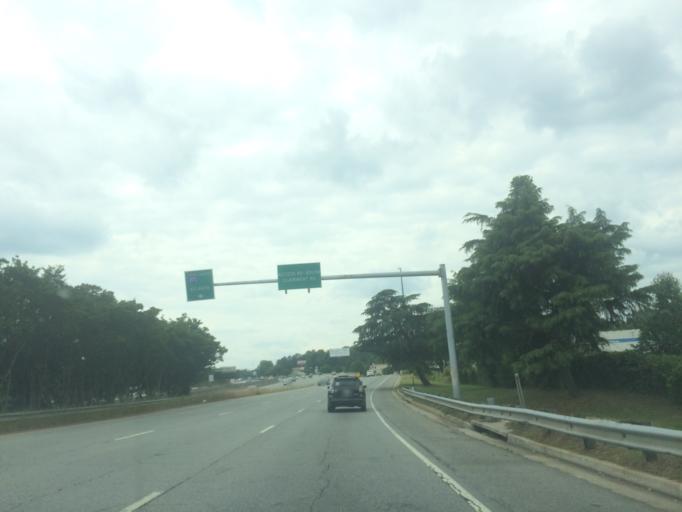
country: US
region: Georgia
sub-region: DeKalb County
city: Chamblee
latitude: 33.8638
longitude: -84.2903
